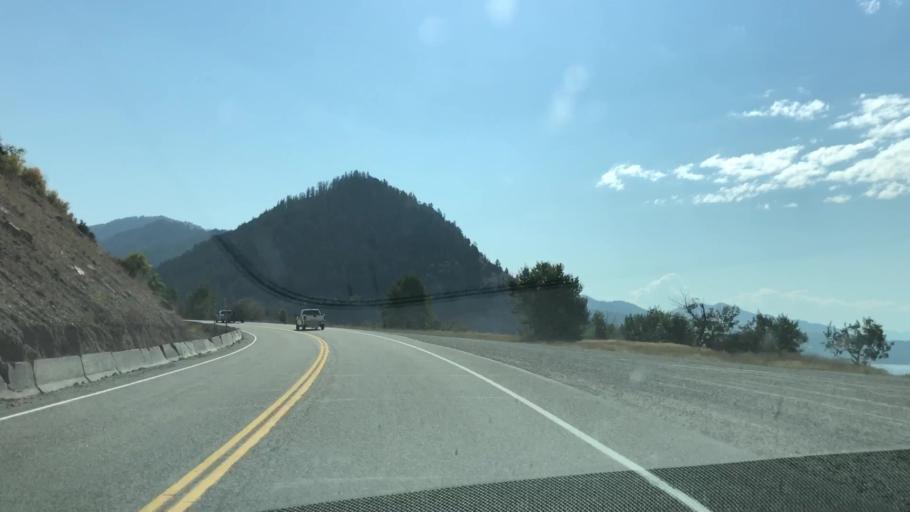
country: US
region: Idaho
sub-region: Teton County
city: Victor
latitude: 43.3192
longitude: -111.1549
